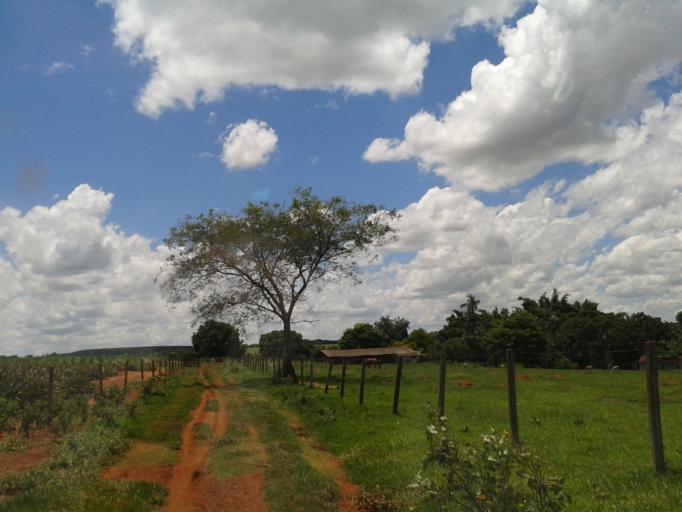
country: BR
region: Minas Gerais
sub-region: Centralina
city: Centralina
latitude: -18.7028
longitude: -49.1621
